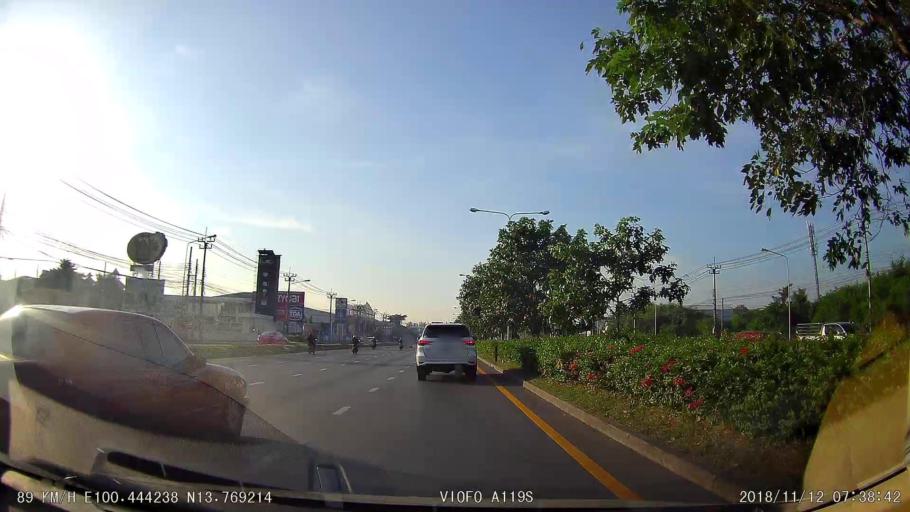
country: TH
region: Bangkok
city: Taling Chan
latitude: 13.7684
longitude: 100.4443
